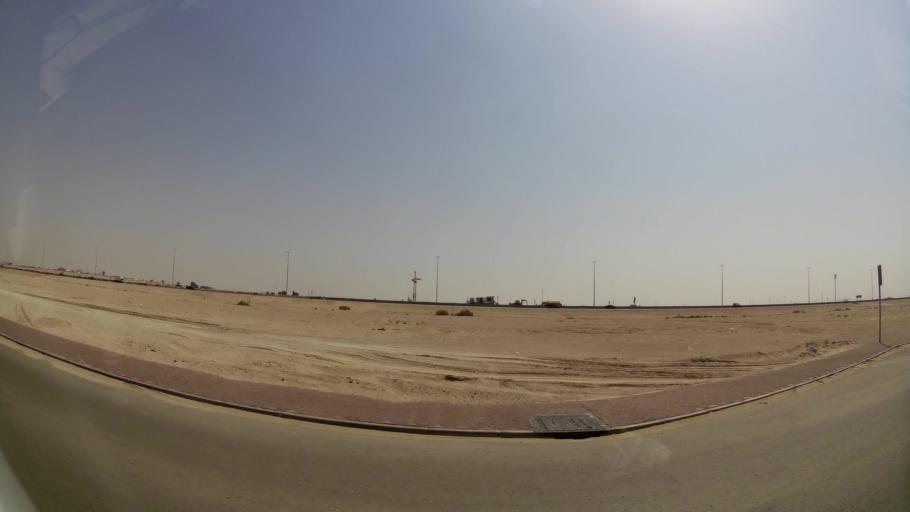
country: AE
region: Abu Dhabi
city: Abu Dhabi
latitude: 24.2996
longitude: 54.5814
